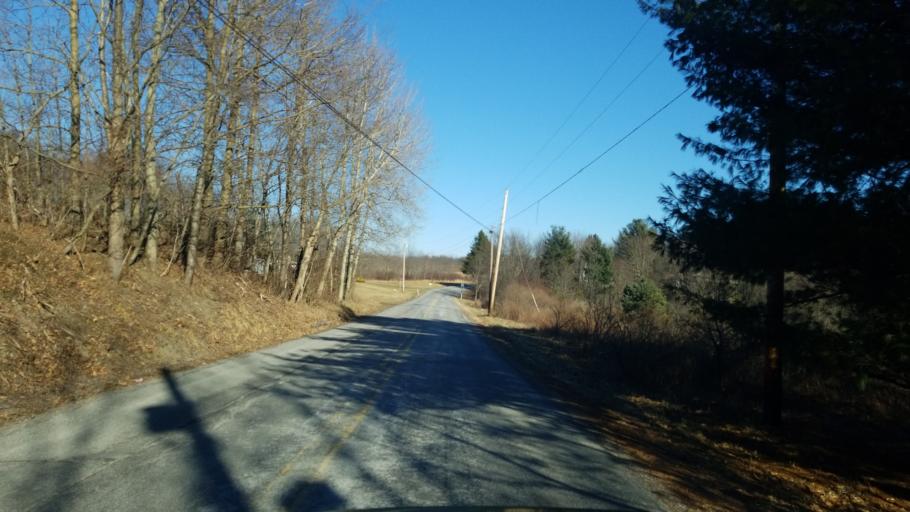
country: US
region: Pennsylvania
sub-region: Clearfield County
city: Sandy
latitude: 41.0480
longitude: -78.7553
